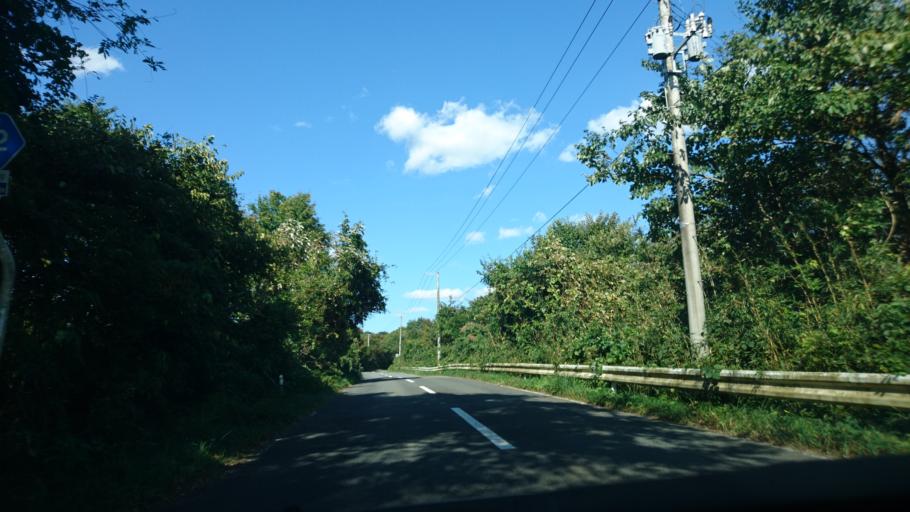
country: JP
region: Iwate
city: Ichinoseki
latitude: 38.8484
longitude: 141.0346
